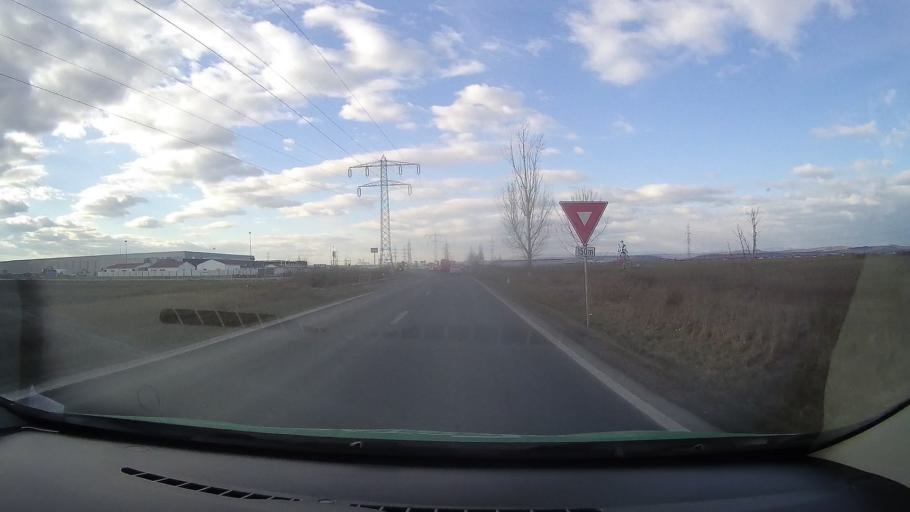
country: RO
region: Dambovita
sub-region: Comuna Comisani
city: Lazuri
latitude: 44.8740
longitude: 25.5209
